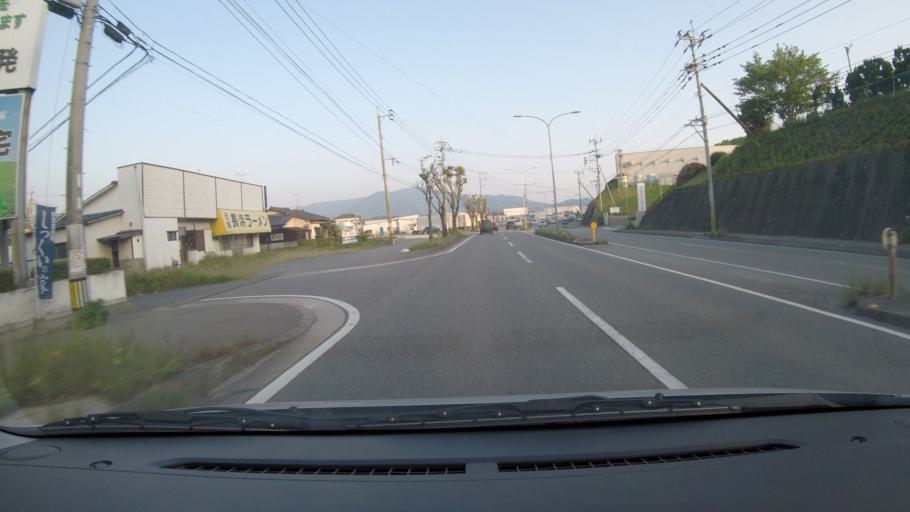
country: JP
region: Fukuoka
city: Sasaguri
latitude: 33.6475
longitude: 130.4959
